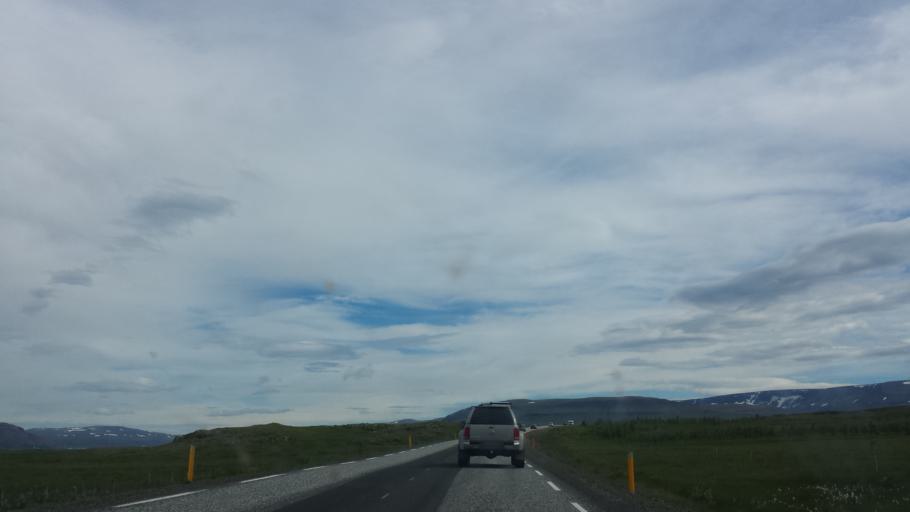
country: IS
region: West
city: Borgarnes
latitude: 64.3736
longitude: -21.8412
